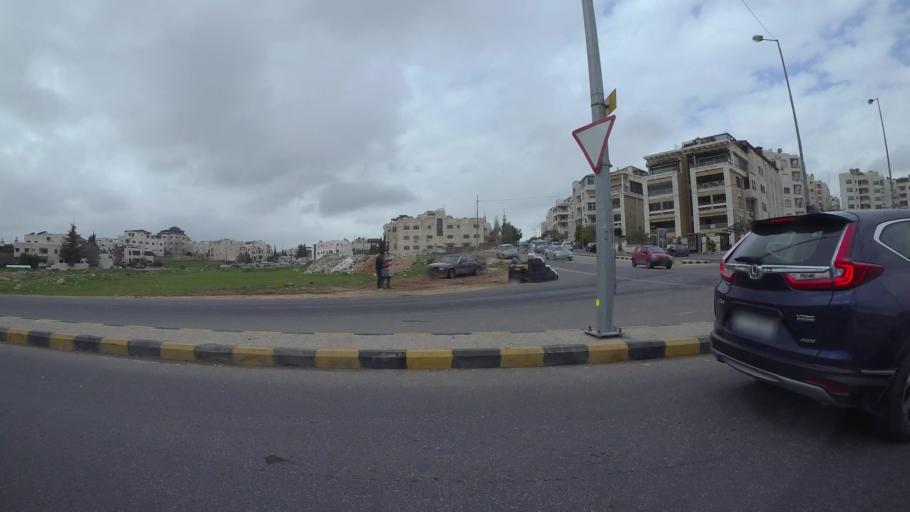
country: JO
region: Amman
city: Wadi as Sir
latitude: 31.9832
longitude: 35.8377
